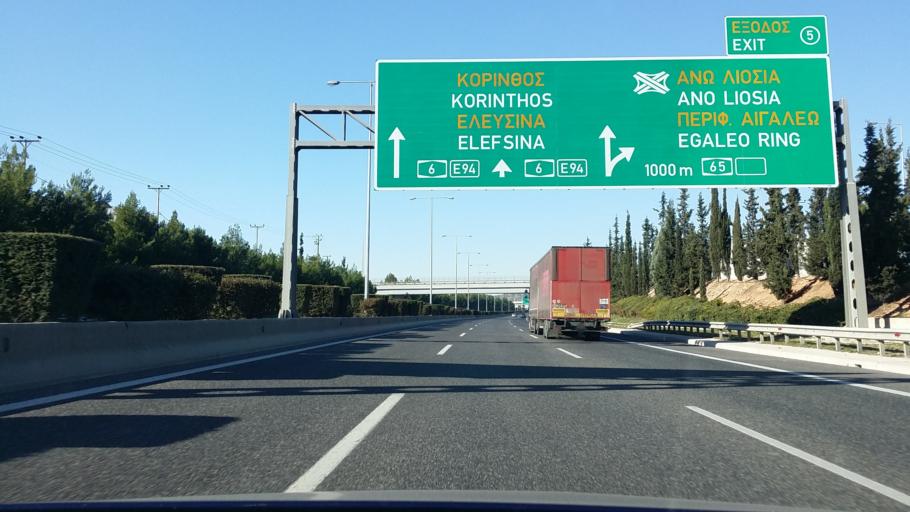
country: GR
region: Attica
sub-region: Nomarchia Dytikis Attikis
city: Ano Liosia
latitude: 38.0731
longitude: 23.6939
